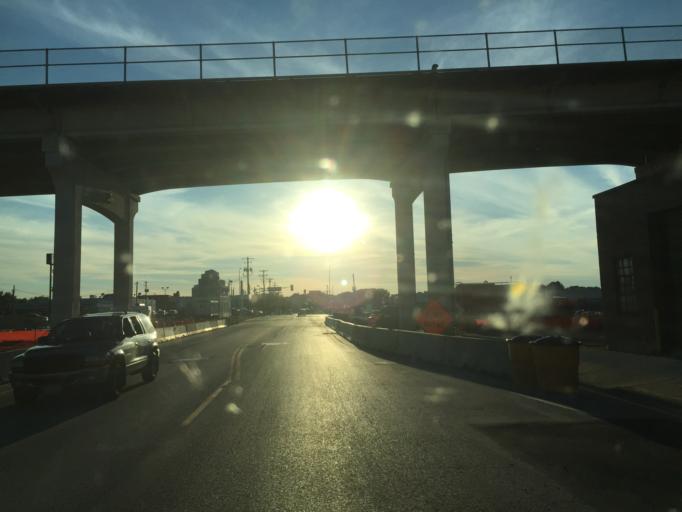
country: US
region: Minnesota
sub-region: Winona County
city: Winona
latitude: 44.0547
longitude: -91.6410
